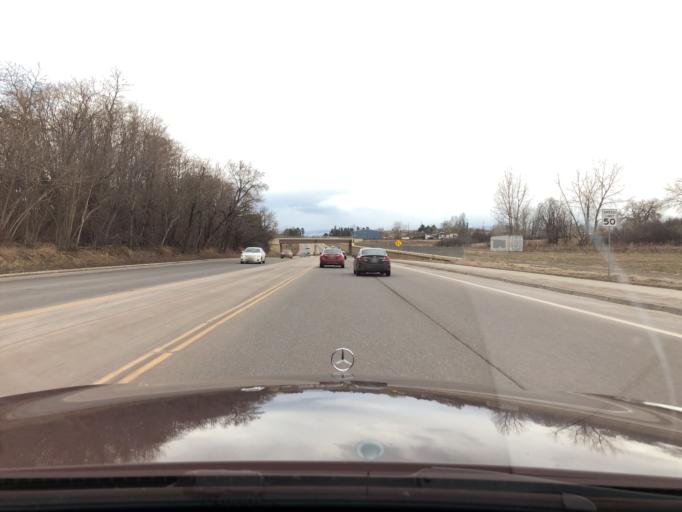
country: US
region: Colorado
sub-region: Boulder County
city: Gunbarrel
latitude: 40.0147
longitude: -105.1807
